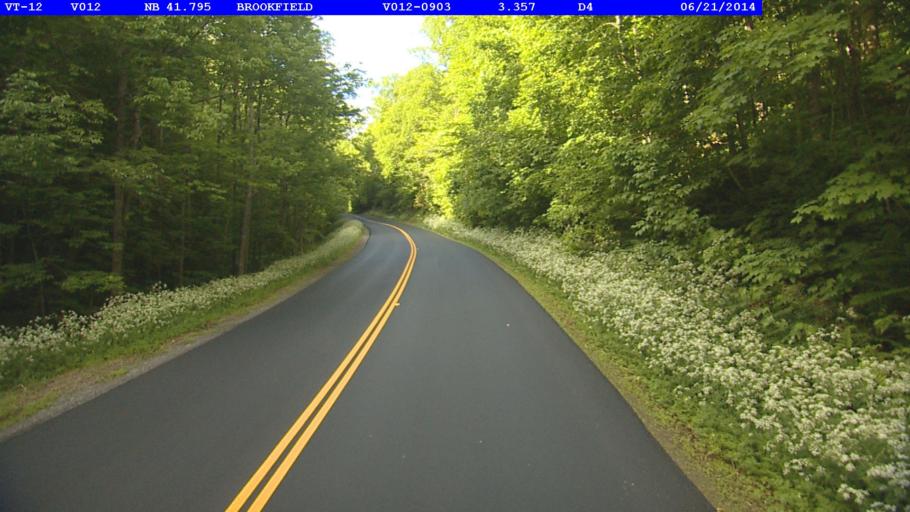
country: US
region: Vermont
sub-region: Washington County
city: Northfield
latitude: 44.0506
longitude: -72.6429
